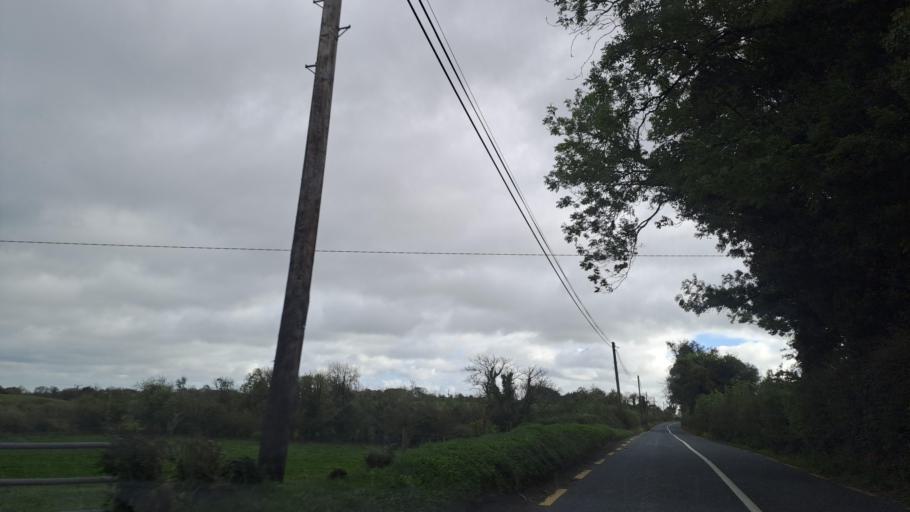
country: IE
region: Ulster
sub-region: An Cabhan
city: Kingscourt
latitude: 53.9140
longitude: -6.8502
